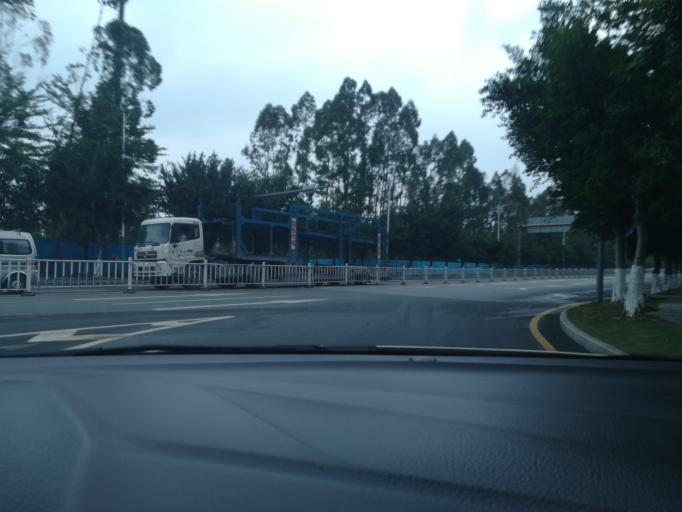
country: CN
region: Guangdong
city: Nansha
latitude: 22.7771
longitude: 113.5969
